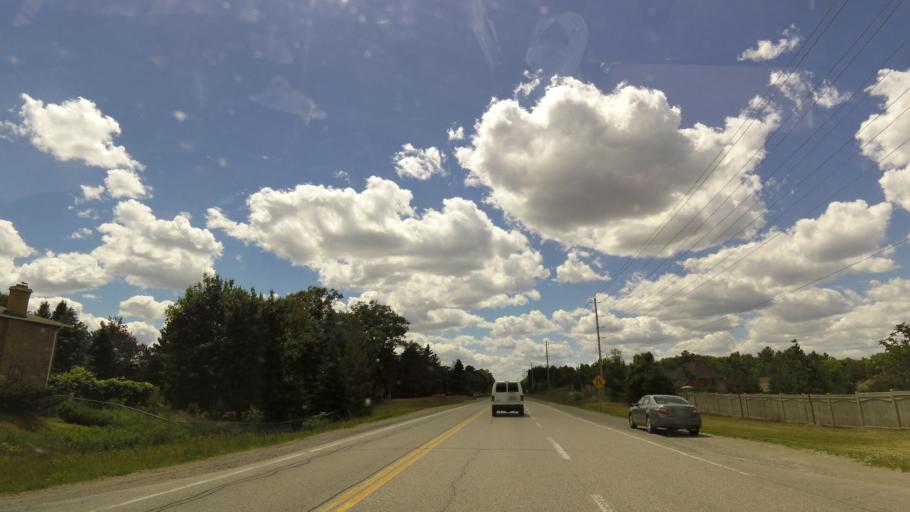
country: CA
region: Ontario
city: Uxbridge
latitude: 44.0434
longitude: -79.1564
